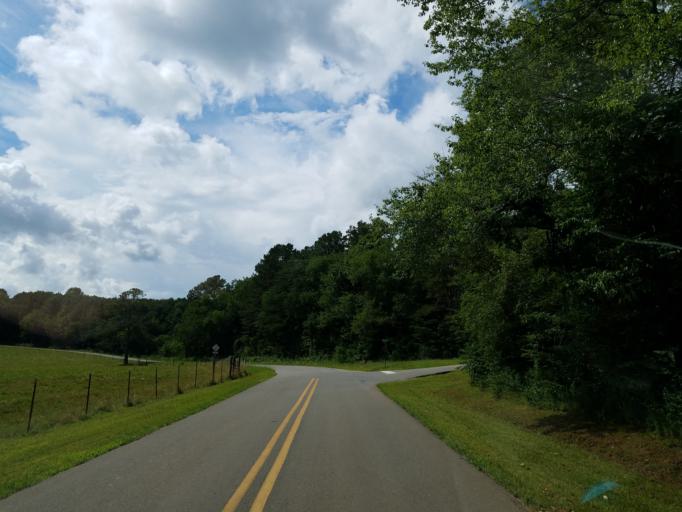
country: US
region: Georgia
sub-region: Pickens County
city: Nelson
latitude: 34.3989
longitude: -84.3743
